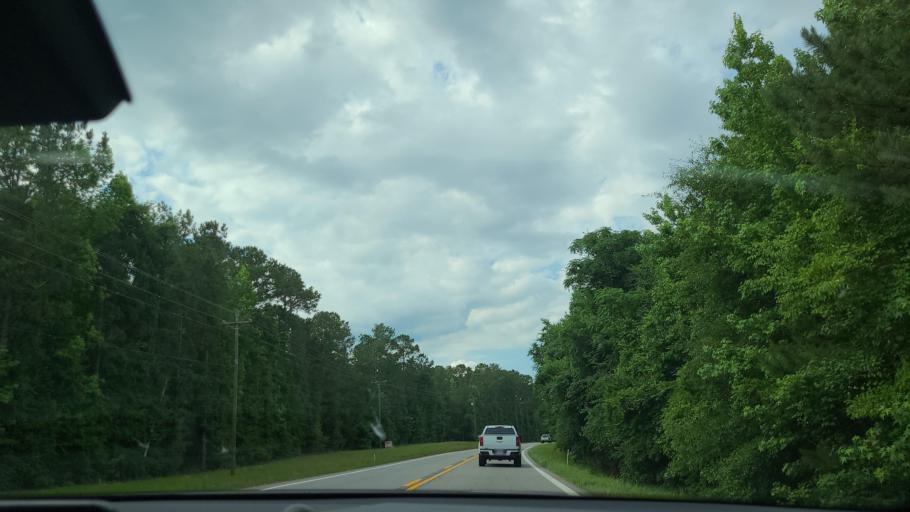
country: US
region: Georgia
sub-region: Putnam County
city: Eatonton
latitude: 33.1746
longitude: -83.4413
